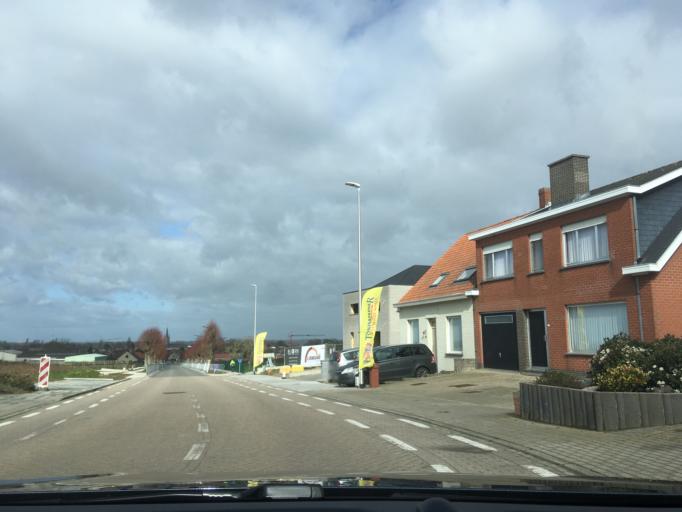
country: BE
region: Flanders
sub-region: Provincie West-Vlaanderen
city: Hooglede
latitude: 50.9893
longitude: 3.1066
